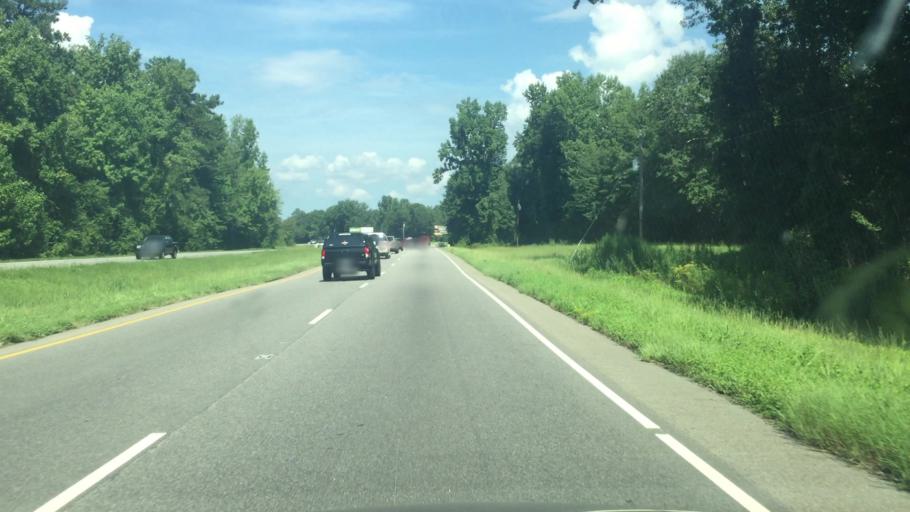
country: US
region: North Carolina
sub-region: Scotland County
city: Laurel Hill
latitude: 34.7968
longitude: -79.5173
